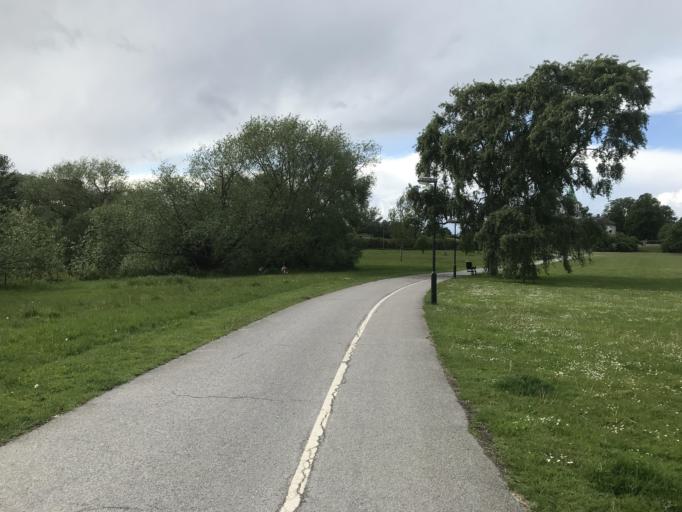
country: SE
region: Skane
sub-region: Burlovs Kommun
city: Arloev
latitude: 55.5762
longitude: 13.0569
